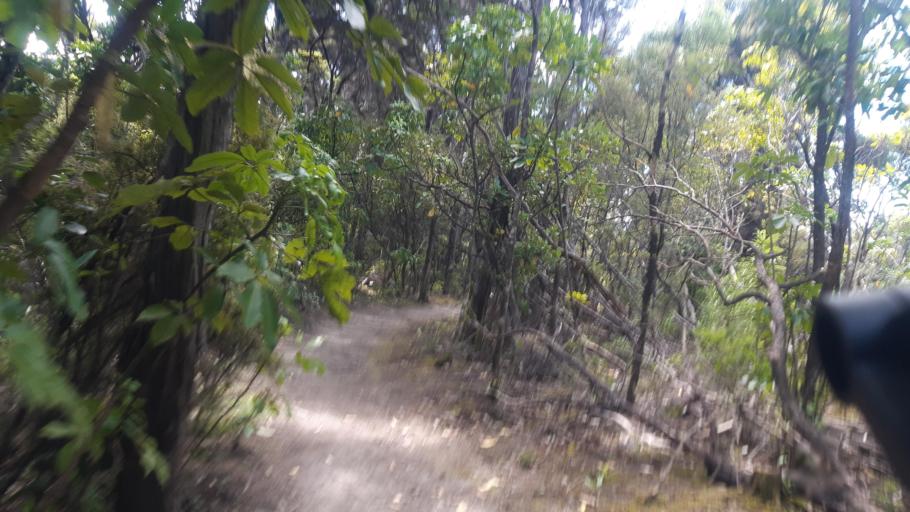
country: NZ
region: Marlborough
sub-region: Marlborough District
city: Picton
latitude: -41.2532
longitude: 174.0443
